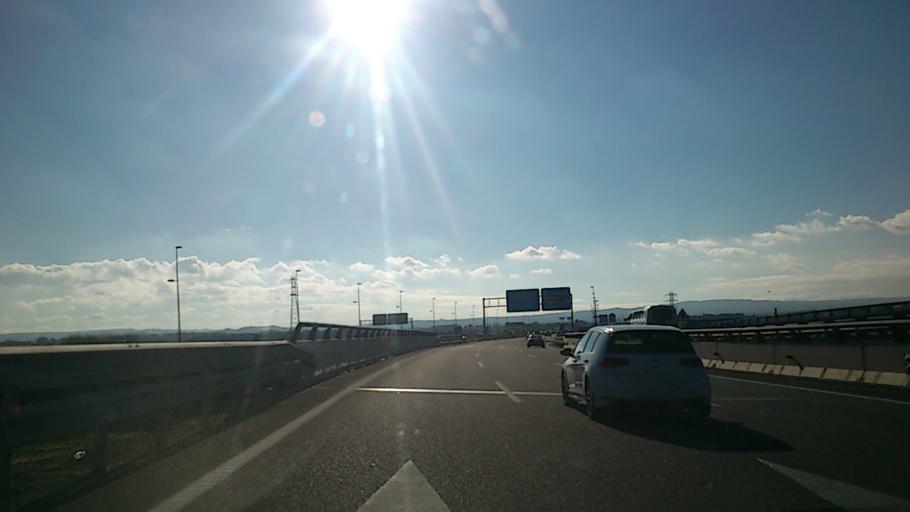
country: ES
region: Aragon
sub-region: Provincia de Zaragoza
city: Almozara
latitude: 41.6761
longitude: -0.9281
